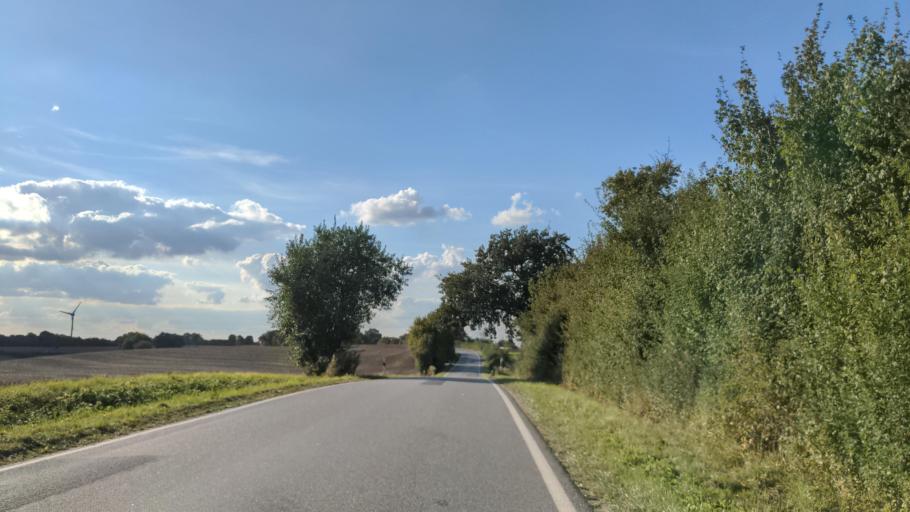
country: DE
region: Schleswig-Holstein
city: Monkhagen
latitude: 53.9459
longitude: 10.5824
